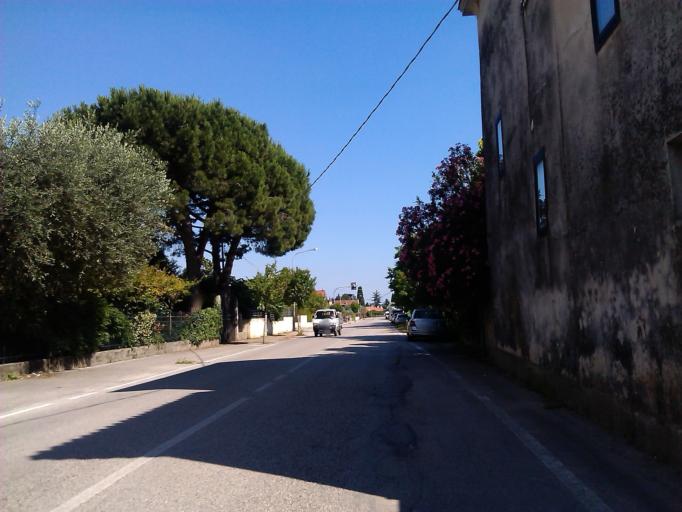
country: IT
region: Veneto
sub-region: Provincia di Vicenza
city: Pove del Grappa
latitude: 45.7925
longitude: 11.7295
